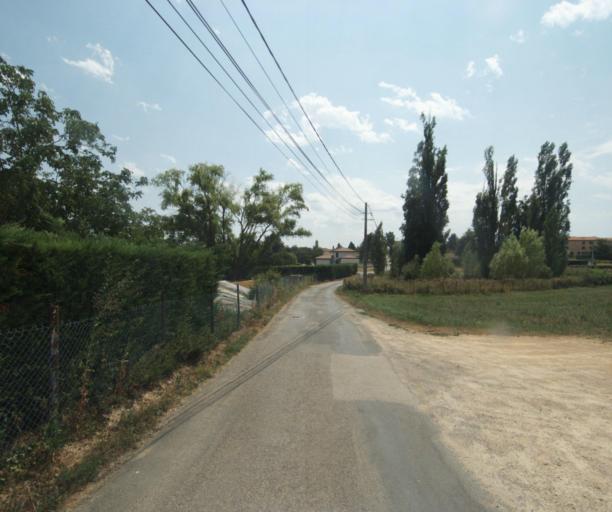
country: FR
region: Rhone-Alpes
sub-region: Departement du Rhone
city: Saint-Germain-Nuelles
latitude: 45.8525
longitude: 4.6152
